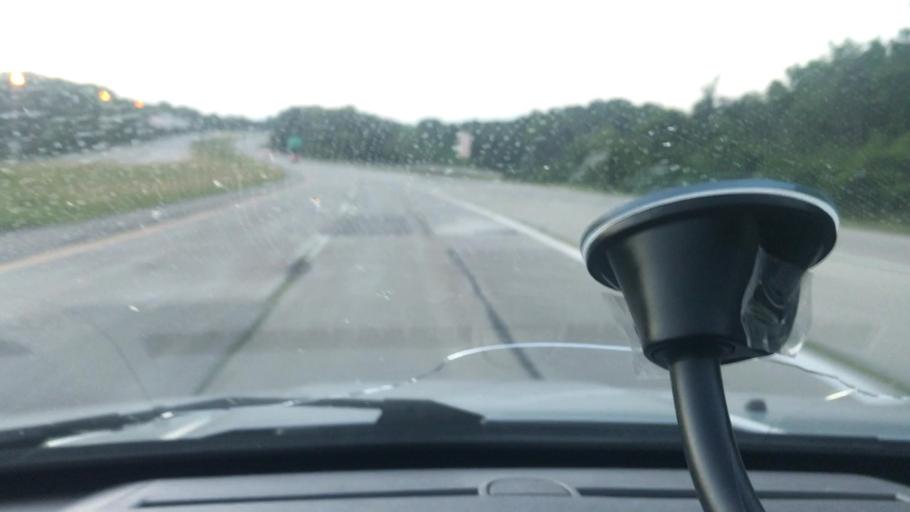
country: US
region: Illinois
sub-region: Peoria County
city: Bellevue
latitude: 40.7462
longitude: -89.6678
